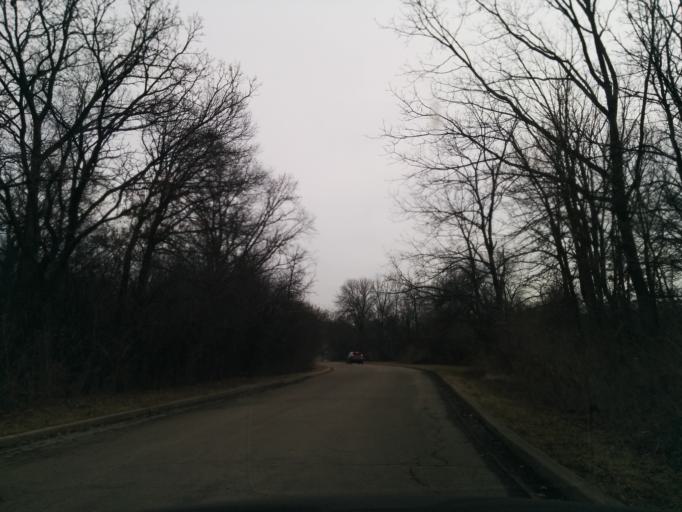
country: US
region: Illinois
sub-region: Cook County
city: Western Springs
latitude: 41.8221
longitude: -87.9050
